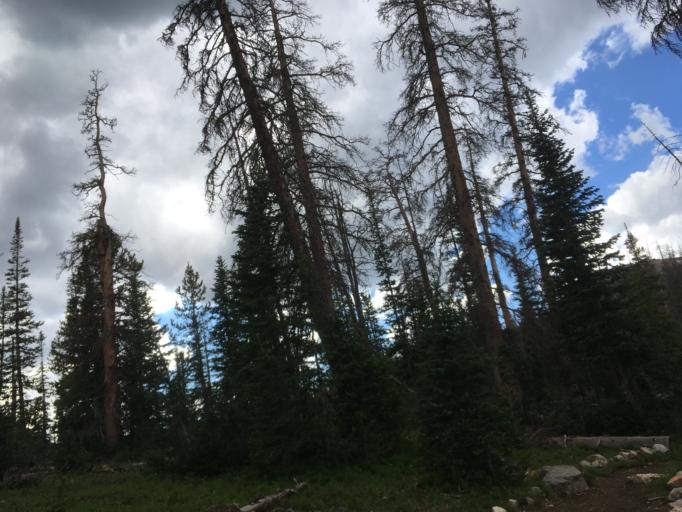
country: US
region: Utah
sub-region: Summit County
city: Kamas
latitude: 40.7167
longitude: -110.8814
